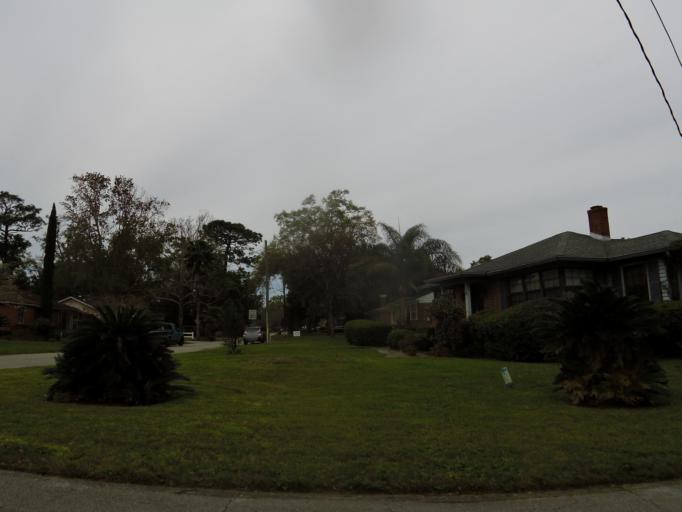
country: US
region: Florida
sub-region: Duval County
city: Jacksonville
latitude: 30.2727
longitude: -81.6466
